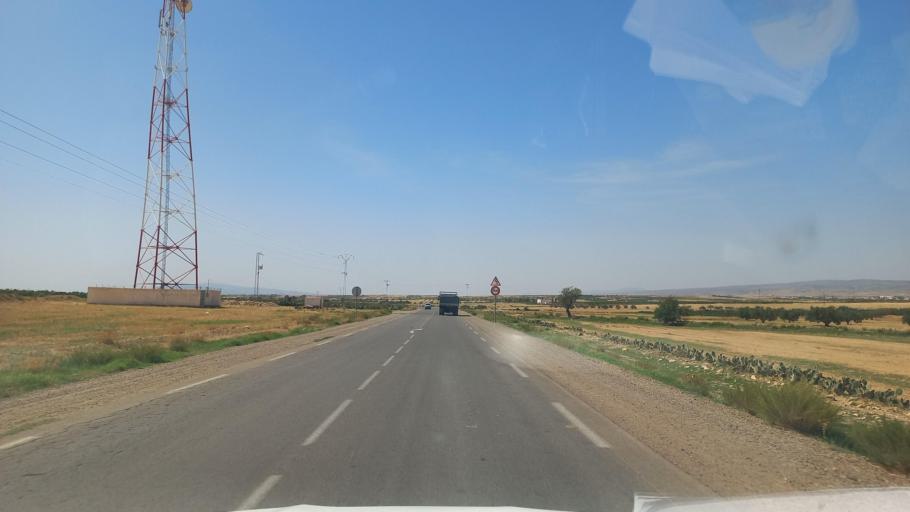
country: TN
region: Al Qasrayn
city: Sbiba
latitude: 35.3752
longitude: 9.1023
